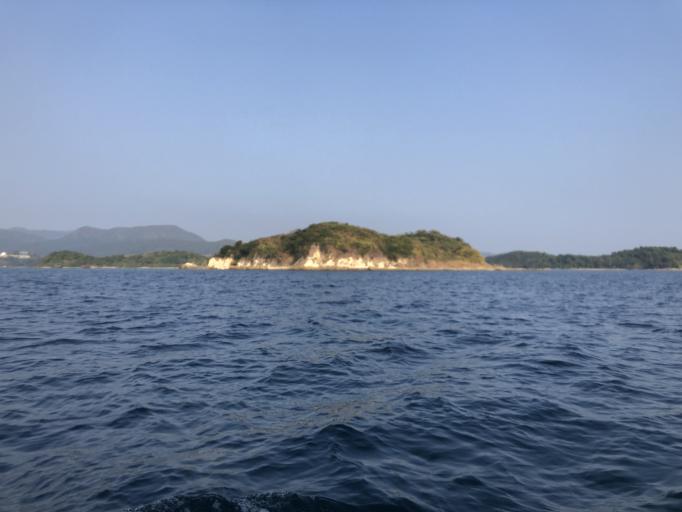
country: HK
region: Sai Kung
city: Sai Kung
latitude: 22.3732
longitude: 114.2823
